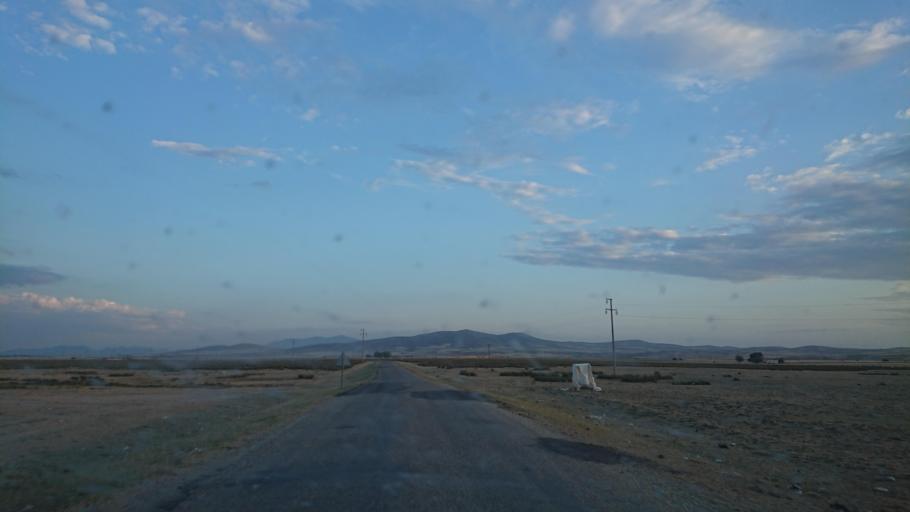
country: TR
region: Aksaray
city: Agacoren
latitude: 38.8857
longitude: 34.0557
